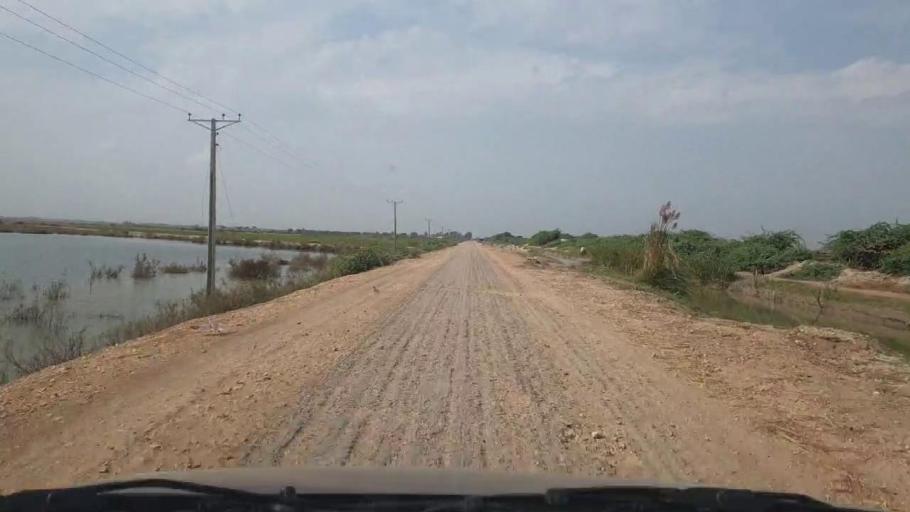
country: PK
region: Sindh
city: Kario
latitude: 24.6250
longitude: 68.5777
